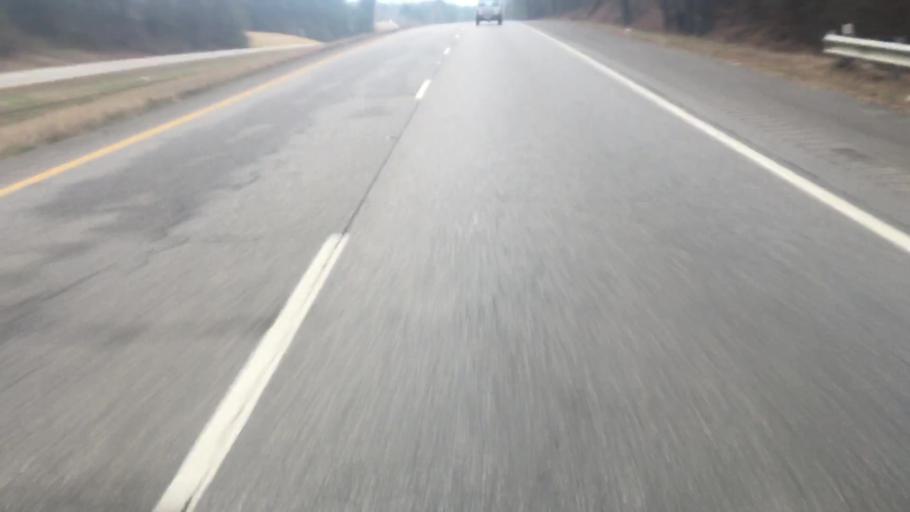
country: US
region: Alabama
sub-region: Walker County
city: Sumiton
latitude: 33.7194
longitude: -87.0001
